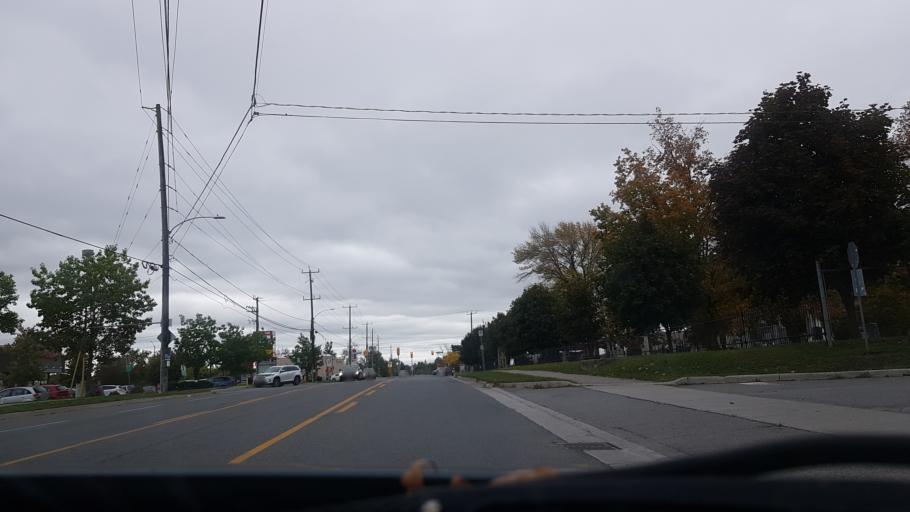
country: CA
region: Ontario
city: Peterborough
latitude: 44.2874
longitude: -78.3305
